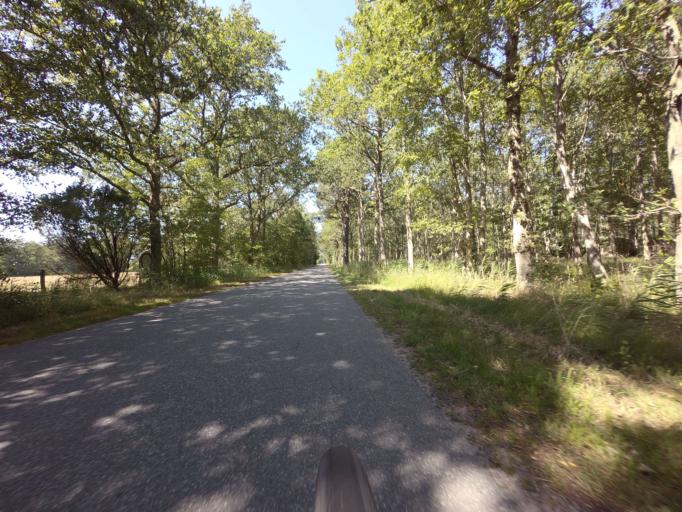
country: DK
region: North Denmark
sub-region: Laeso Kommune
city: Byrum
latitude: 57.2769
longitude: 11.0108
